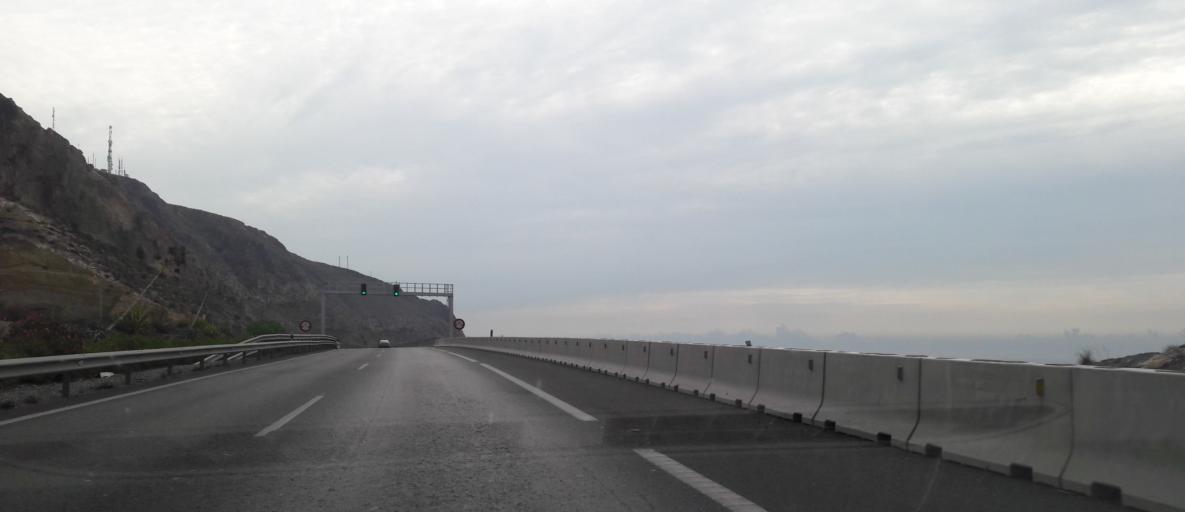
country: ES
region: Andalusia
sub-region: Provincia de Almeria
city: Aguadulce
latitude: 36.8216
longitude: -2.5717
